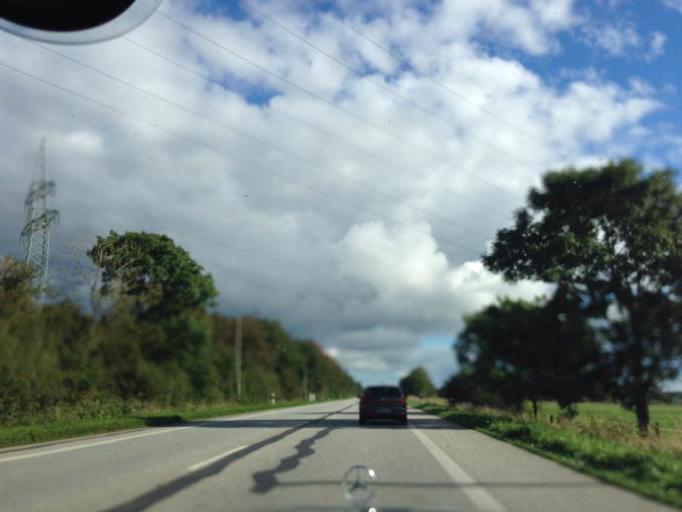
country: DE
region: Schleswig-Holstein
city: Stedesand
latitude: 54.7513
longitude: 8.9032
